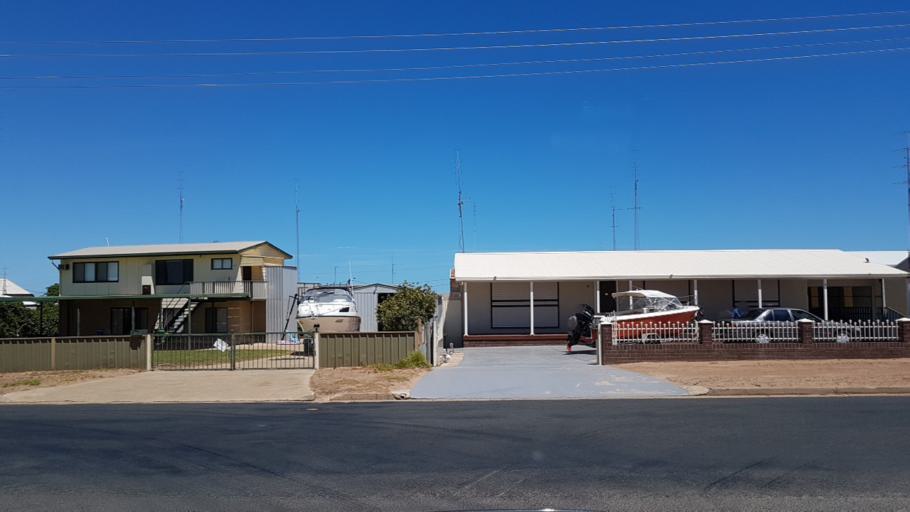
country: AU
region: South Australia
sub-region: Copper Coast
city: Wallaroo
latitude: -33.8952
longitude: 137.6296
